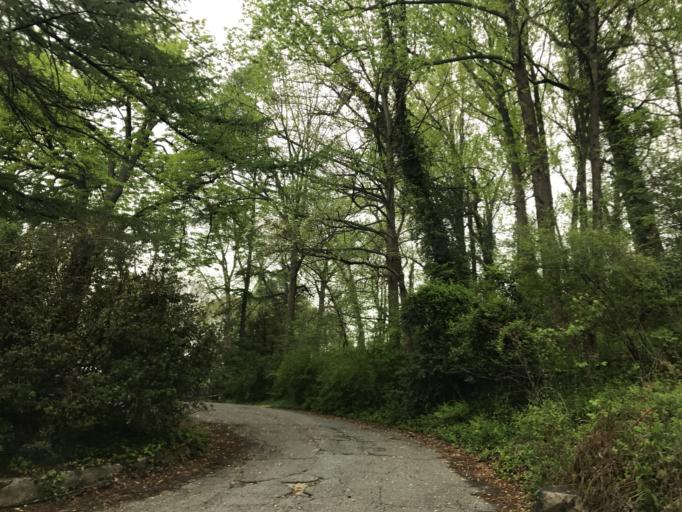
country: US
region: Maryland
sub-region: Baltimore County
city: Towson
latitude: 39.3545
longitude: -76.6406
